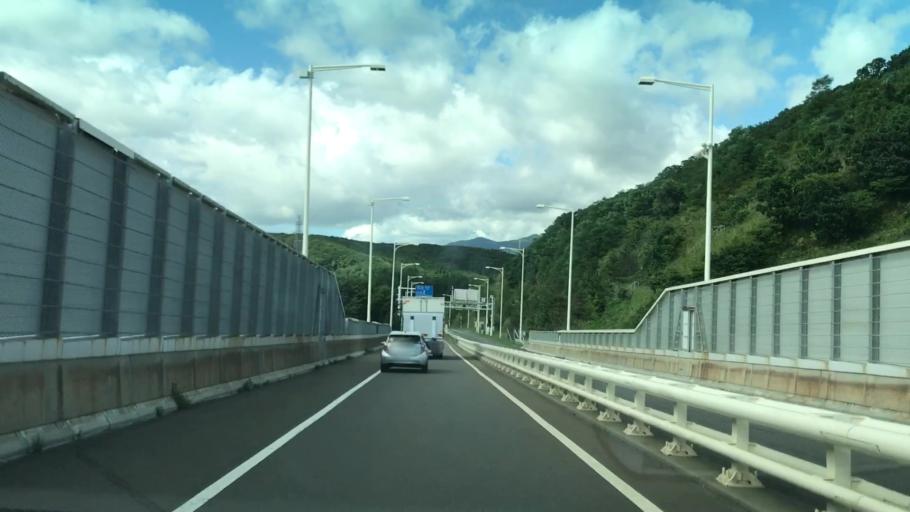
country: JP
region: Hokkaido
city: Muroran
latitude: 42.3620
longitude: 140.9516
